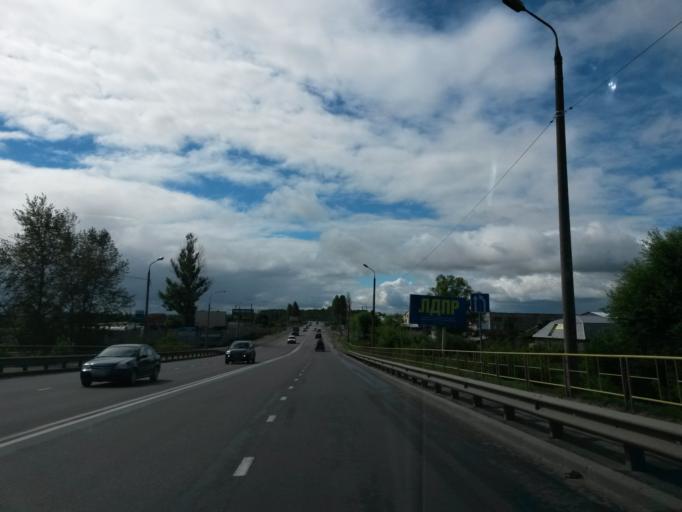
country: RU
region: Jaroslavl
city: Yaroslavl
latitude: 57.6648
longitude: 39.7631
